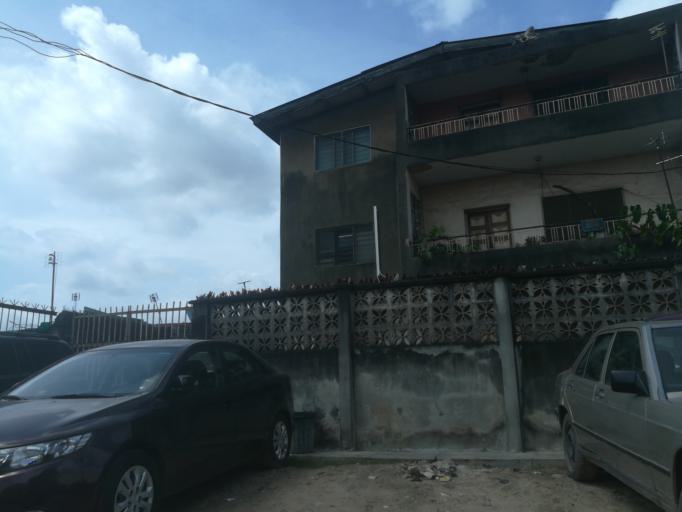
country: NG
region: Lagos
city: Somolu
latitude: 6.5281
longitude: 3.3810
